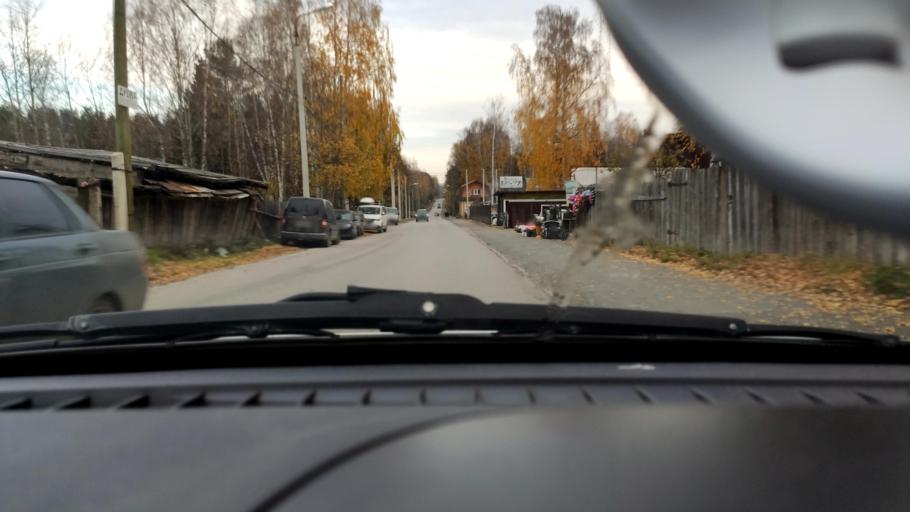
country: RU
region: Perm
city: Kondratovo
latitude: 58.0588
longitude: 56.1240
